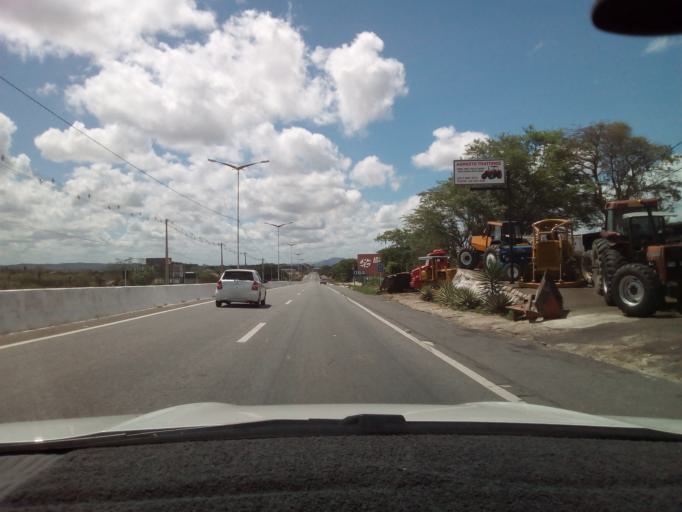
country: BR
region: Paraiba
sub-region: Campina Grande
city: Campina Grande
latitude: -7.2414
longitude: -35.8592
